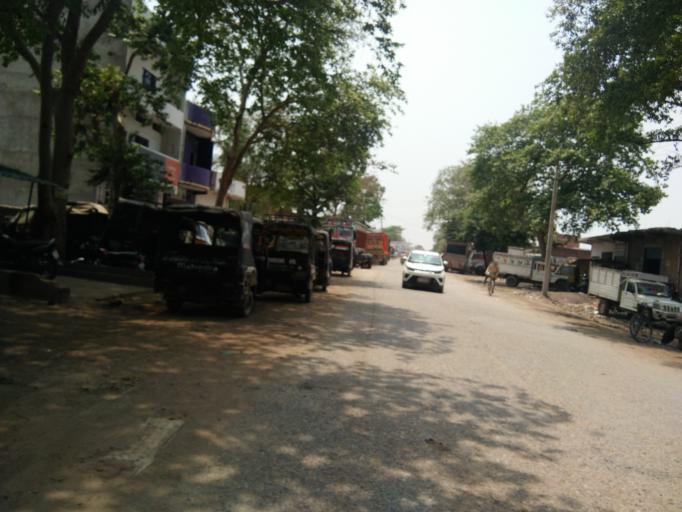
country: IN
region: Uttar Pradesh
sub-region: Ghazipur
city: Zamania
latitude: 25.4338
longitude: 83.6743
